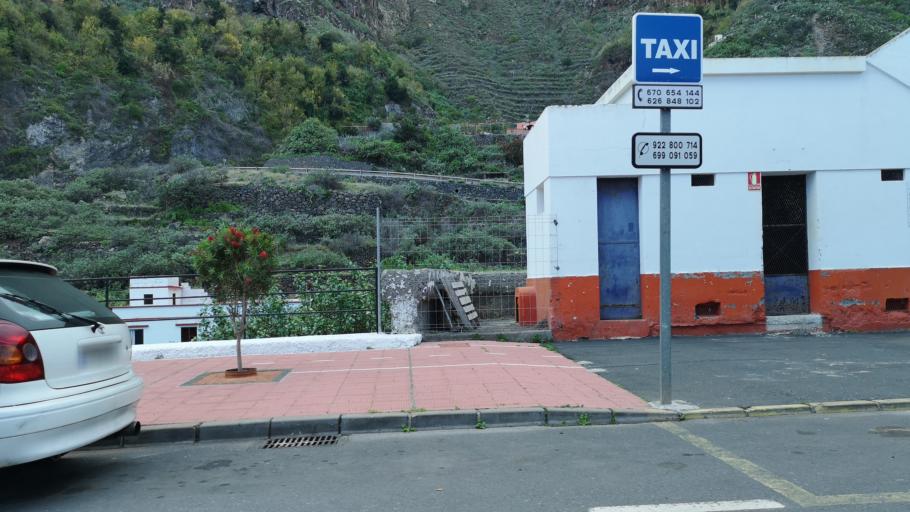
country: ES
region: Canary Islands
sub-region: Provincia de Santa Cruz de Tenerife
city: Agulo
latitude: 28.1862
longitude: -17.1950
